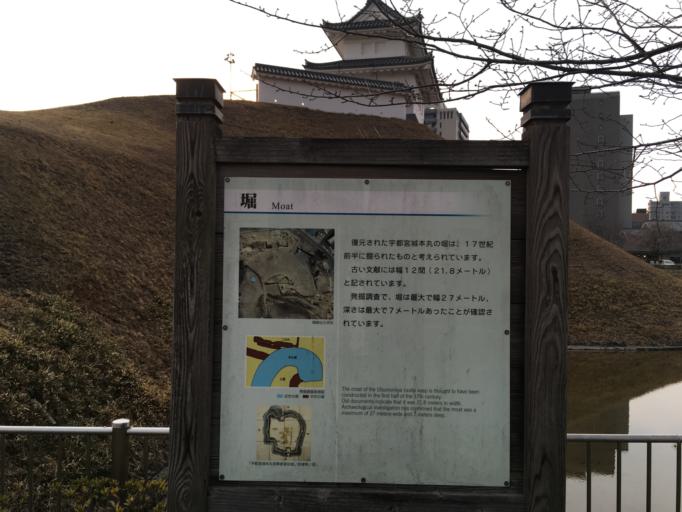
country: JP
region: Tochigi
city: Utsunomiya-shi
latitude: 36.5554
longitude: 139.8855
